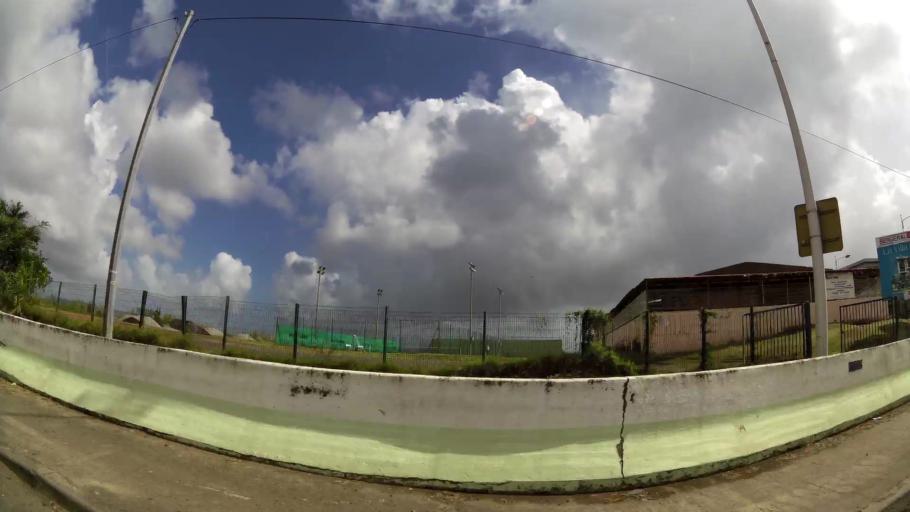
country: MQ
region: Martinique
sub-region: Martinique
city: Fort-de-France
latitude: 14.6045
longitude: -61.0424
